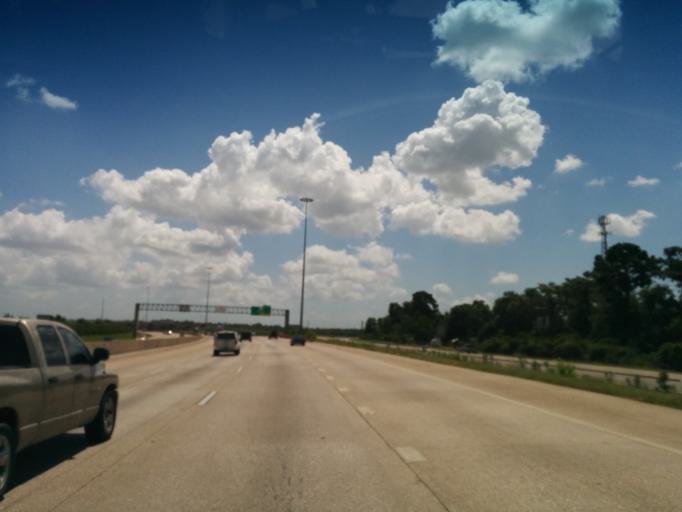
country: US
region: Texas
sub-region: Harris County
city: Highlands
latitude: 29.7903
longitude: -95.0548
